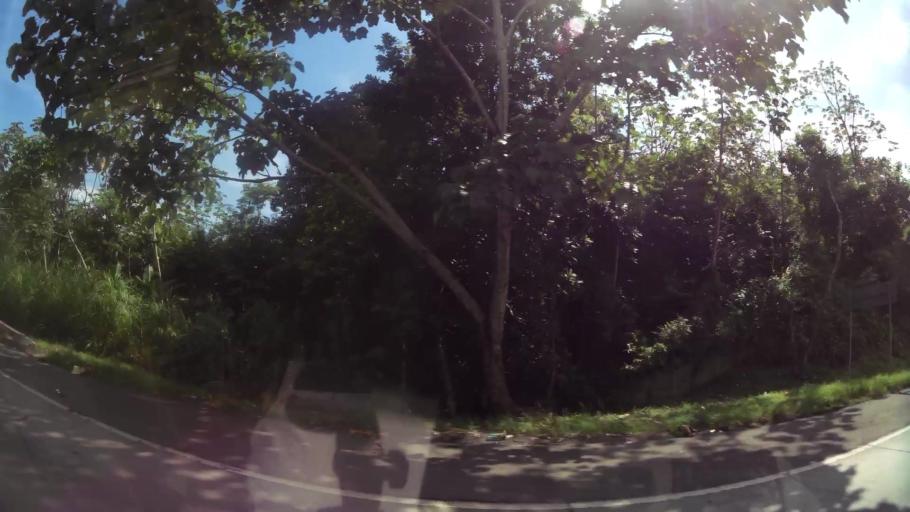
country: PA
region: Panama
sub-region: Distrito de Panama
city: Paraiso
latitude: 9.0275
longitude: -79.5992
